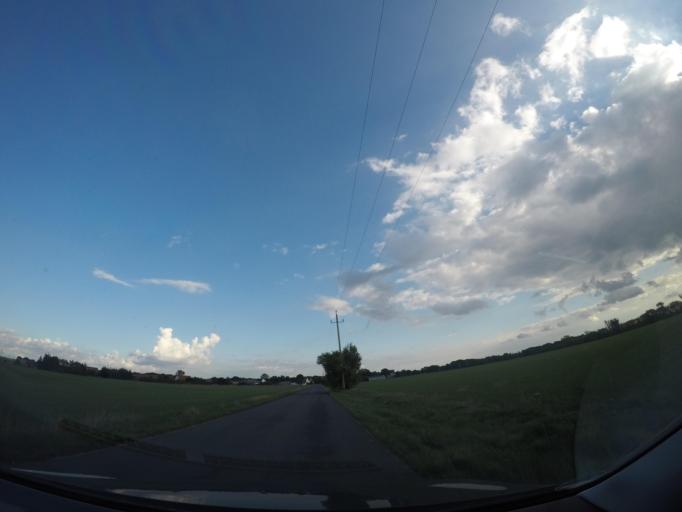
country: DE
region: Saxony-Anhalt
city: Kusey
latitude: 52.5681
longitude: 11.1271
